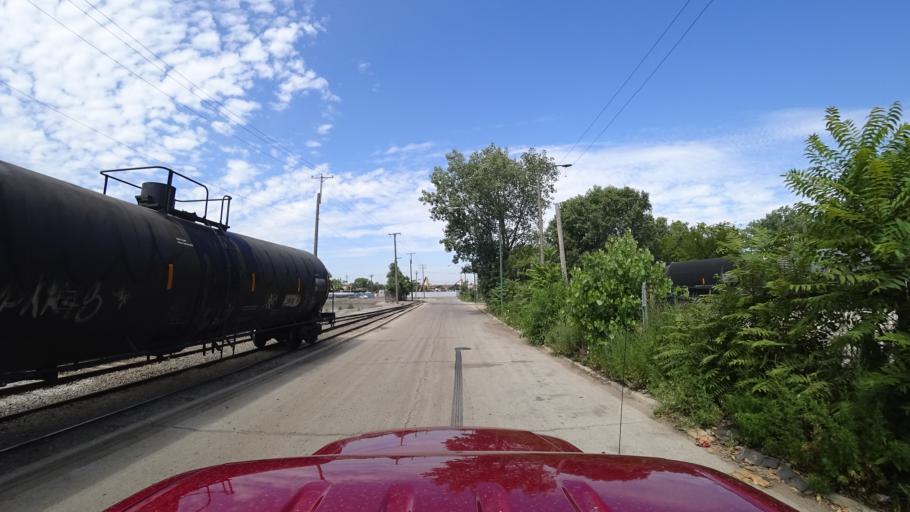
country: US
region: Illinois
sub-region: Cook County
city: Chicago
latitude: 41.8252
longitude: -87.6535
